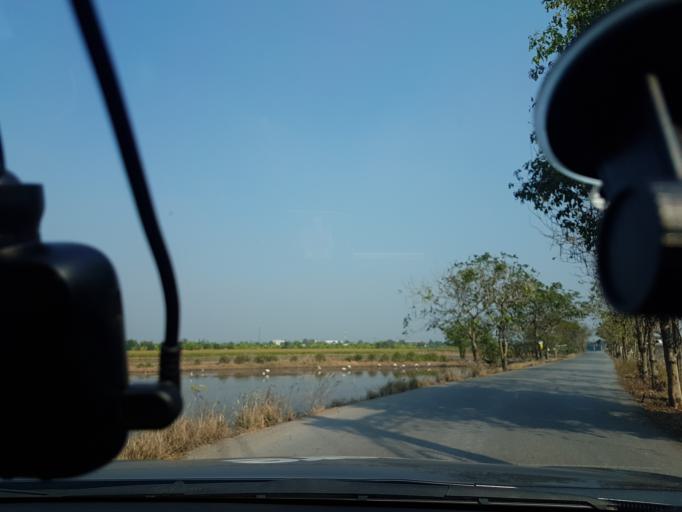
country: TH
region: Pathum Thani
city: Lam Luk Ka
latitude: 13.9135
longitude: 100.7096
